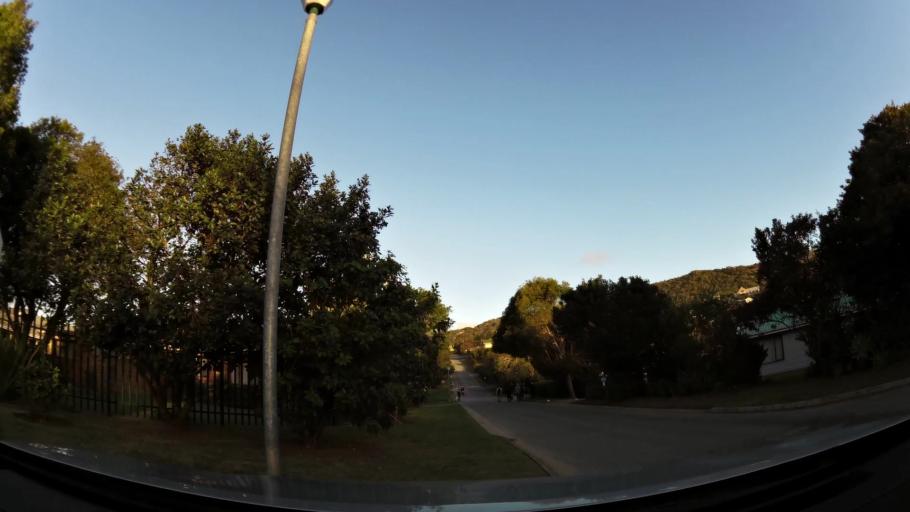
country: ZA
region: Western Cape
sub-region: Eden District Municipality
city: Knysna
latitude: -34.0200
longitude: 22.8119
